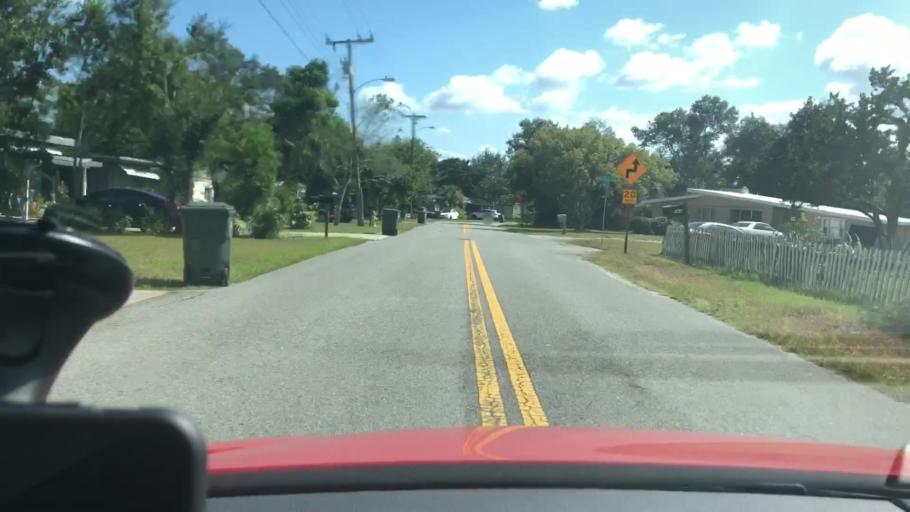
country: US
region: Florida
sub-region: Volusia County
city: Daytona Beach
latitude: 29.2087
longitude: -81.0560
